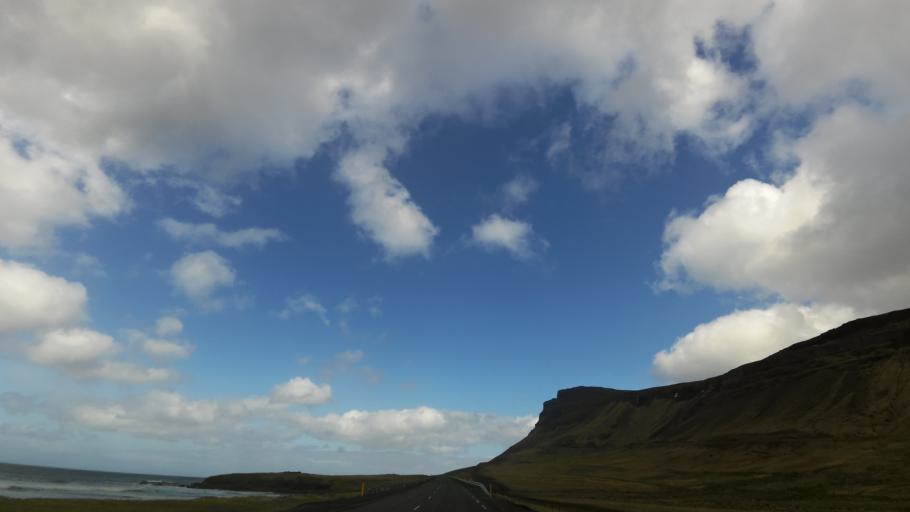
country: IS
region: West
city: Olafsvik
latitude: 64.9315
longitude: -23.5076
